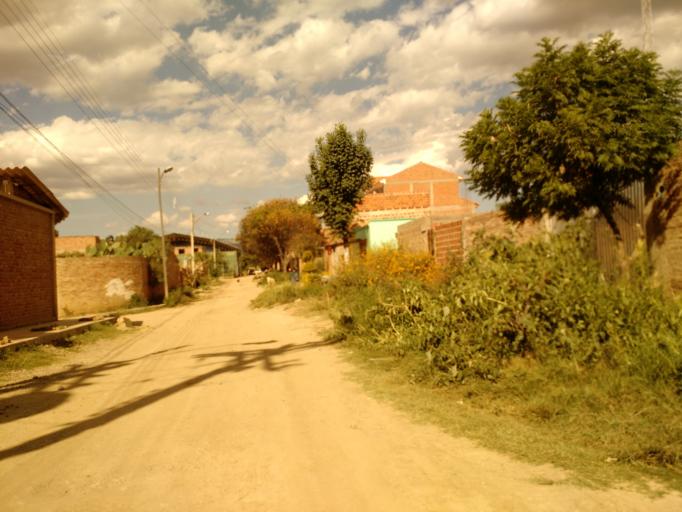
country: BO
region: Cochabamba
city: Cochabamba
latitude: -17.4582
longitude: -66.1564
